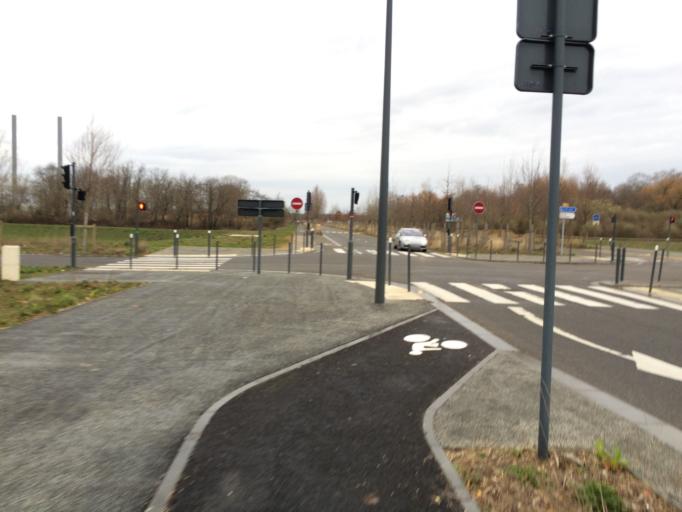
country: FR
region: Ile-de-France
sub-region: Departement de l'Essonne
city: Vauhallan
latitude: 48.7179
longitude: 2.2028
